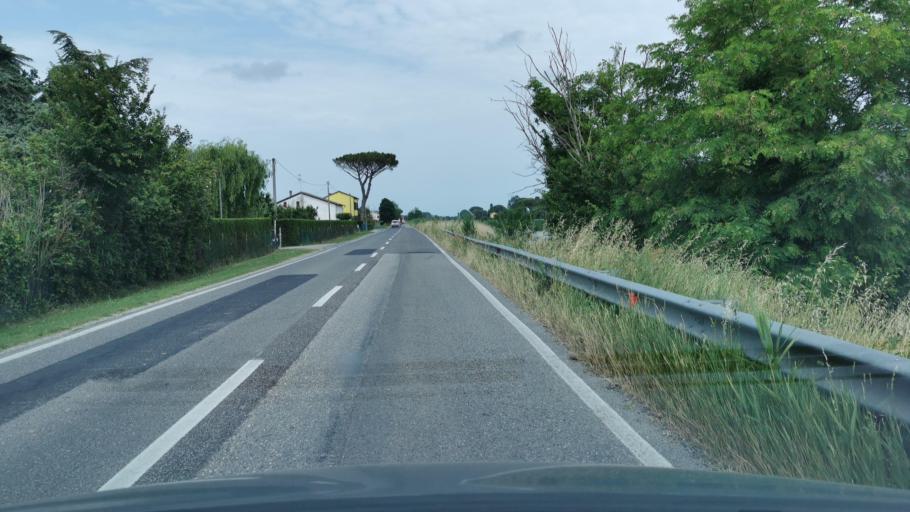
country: IT
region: Emilia-Romagna
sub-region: Provincia di Ravenna
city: Sant'Alberto
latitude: 44.5477
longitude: 12.2142
